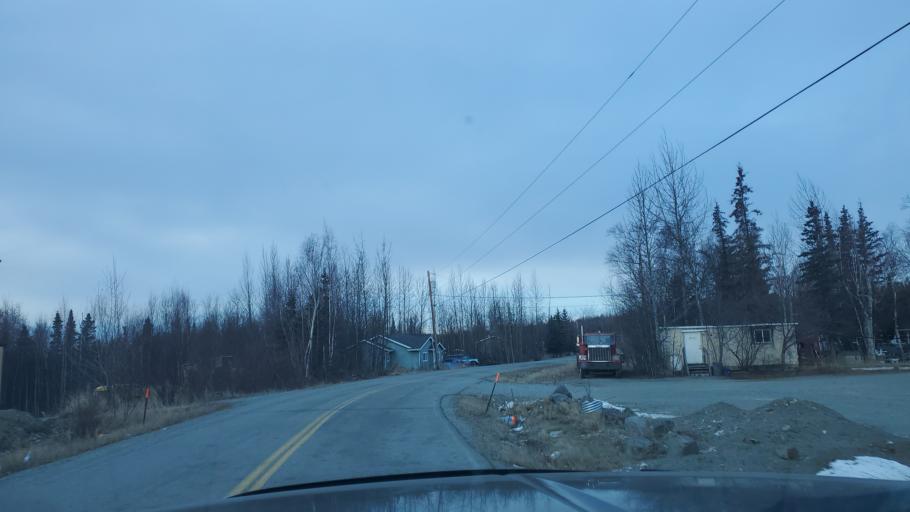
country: US
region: Alaska
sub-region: Matanuska-Susitna Borough
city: Lakes
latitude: 61.5724
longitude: -149.3339
